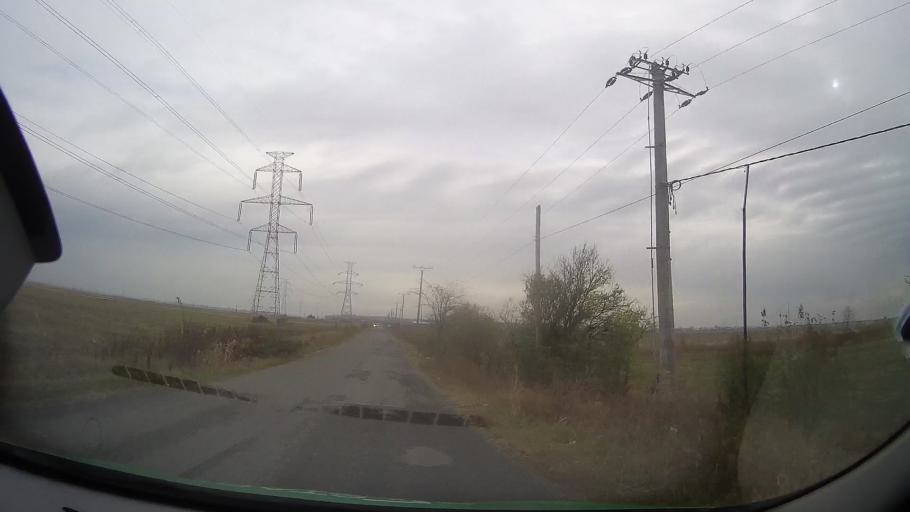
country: RO
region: Prahova
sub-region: Comuna Valea Calugareasca
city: Pantazi
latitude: 44.9283
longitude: 26.1487
